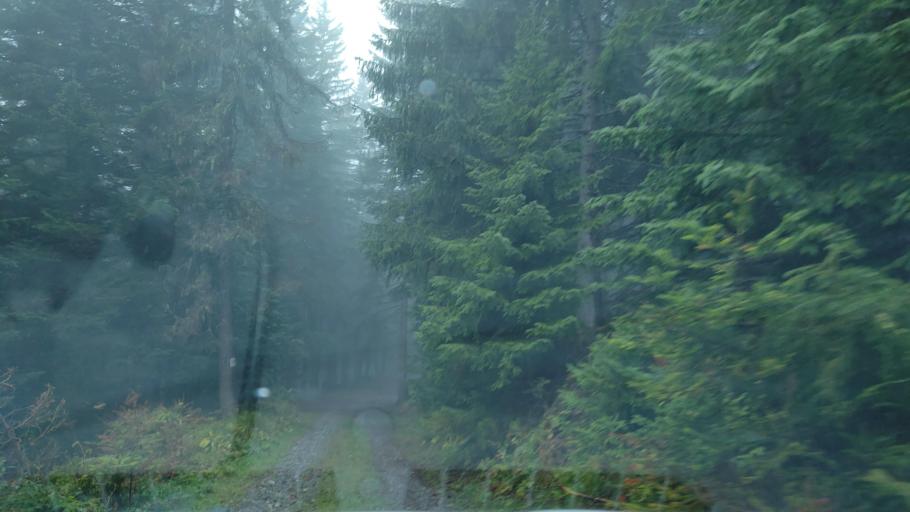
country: IT
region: Piedmont
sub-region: Provincia di Torino
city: Moncenisio
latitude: 45.2938
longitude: 6.8263
